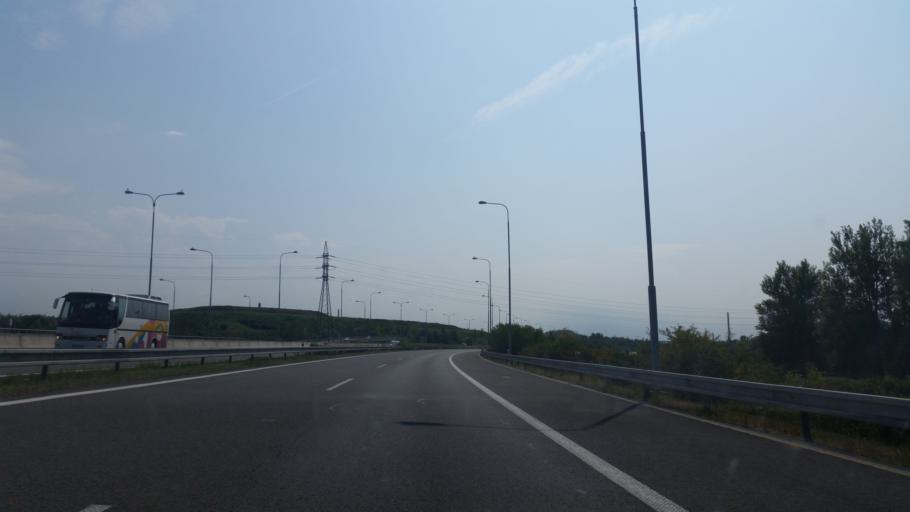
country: PL
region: Silesian Voivodeship
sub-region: Powiat raciborski
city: Chalupki
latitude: 49.8798
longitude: 18.3047
